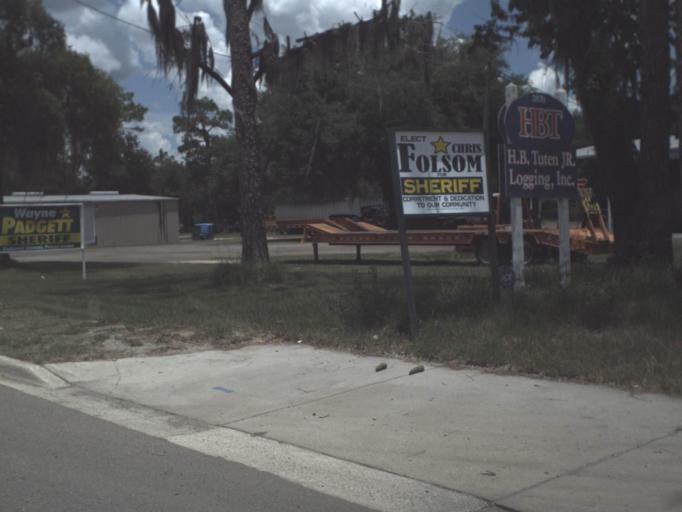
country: US
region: Florida
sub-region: Taylor County
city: Perry
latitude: 30.0710
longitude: -83.5609
